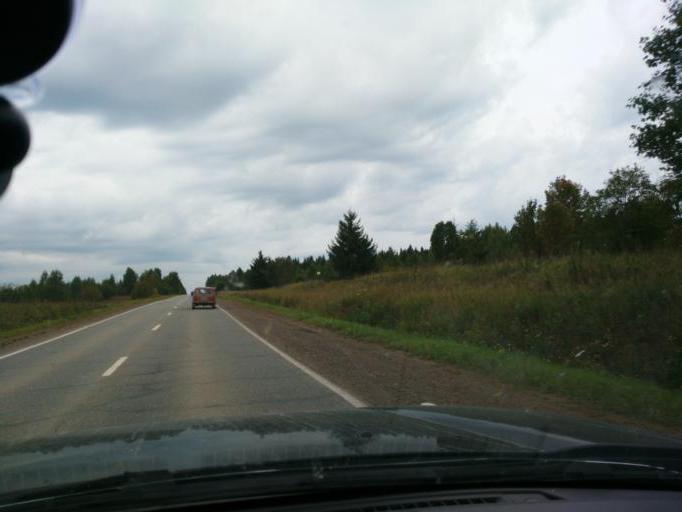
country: RU
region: Perm
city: Chernushka
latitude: 56.7523
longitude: 56.1503
